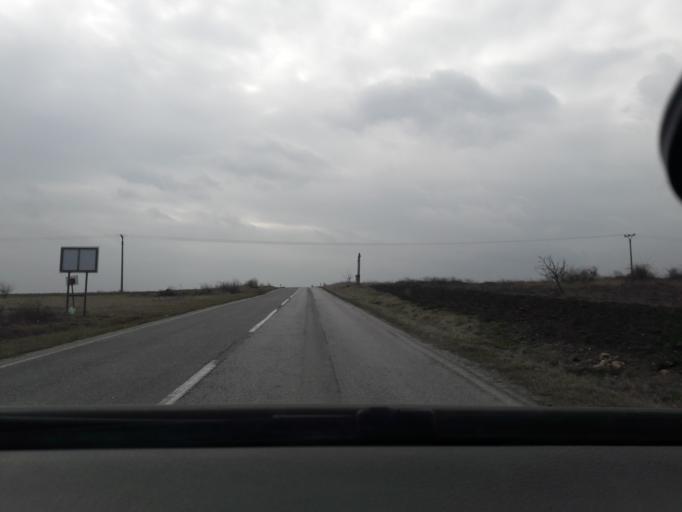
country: SK
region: Trnavsky
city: Smolenice
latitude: 48.4358
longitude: 17.4249
